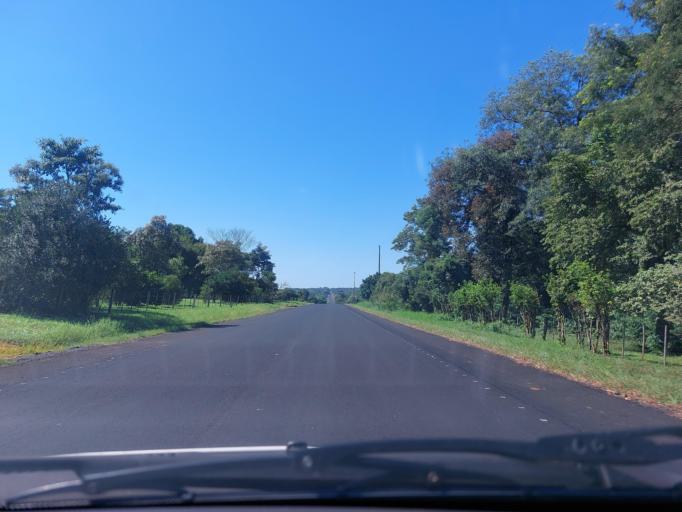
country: PY
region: San Pedro
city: Guayaybi
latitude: -24.5504
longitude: -56.4944
